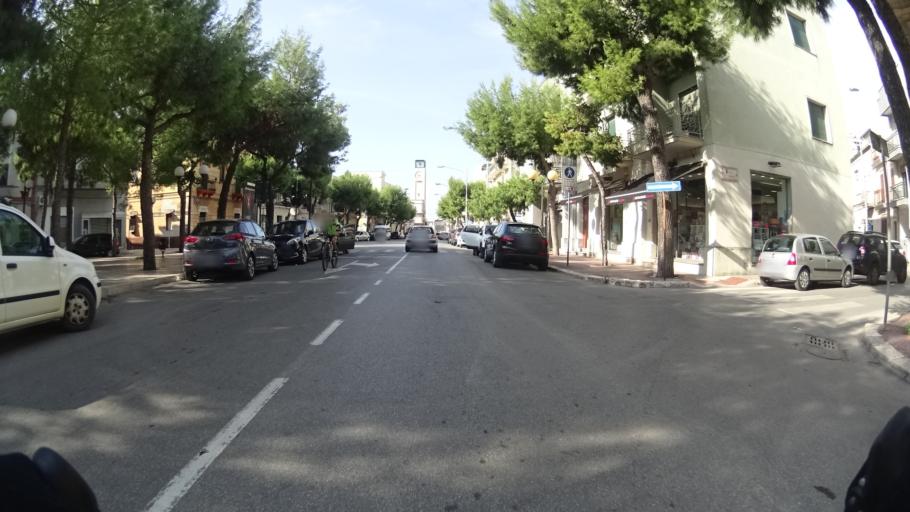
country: IT
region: Apulia
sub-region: Provincia di Taranto
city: Grottaglie
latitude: 40.5363
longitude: 17.4339
